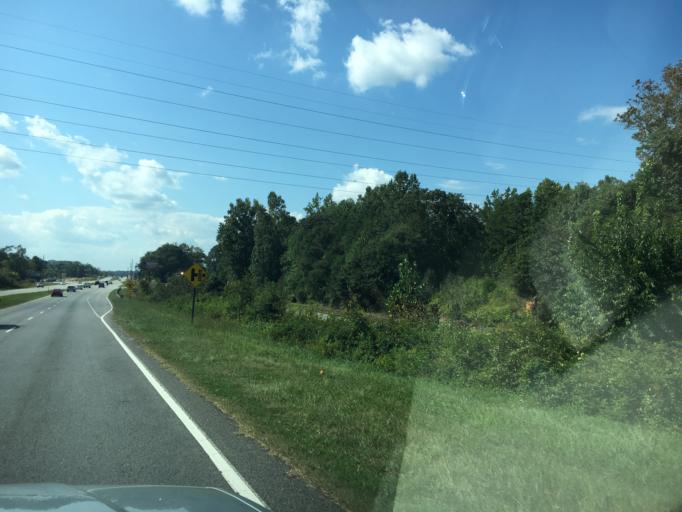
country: US
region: South Carolina
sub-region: Pickens County
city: Clemson
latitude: 34.6918
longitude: -82.8693
